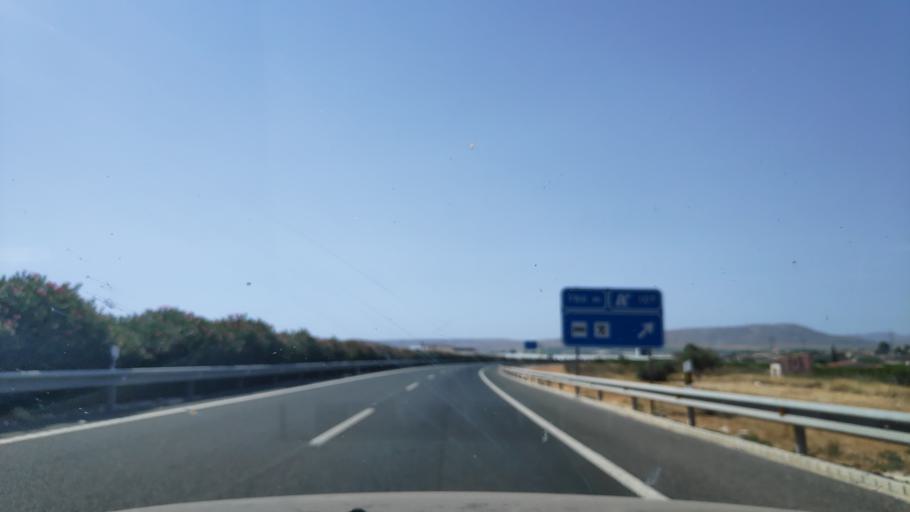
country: ES
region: Murcia
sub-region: Murcia
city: Blanca
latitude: 38.2063
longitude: -1.3486
